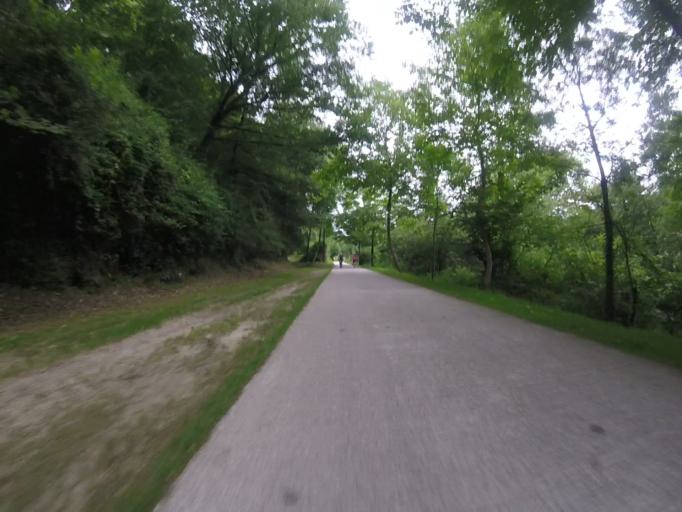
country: ES
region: Navarre
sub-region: Provincia de Navarra
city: Sunbilla
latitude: 43.1564
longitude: -1.6715
